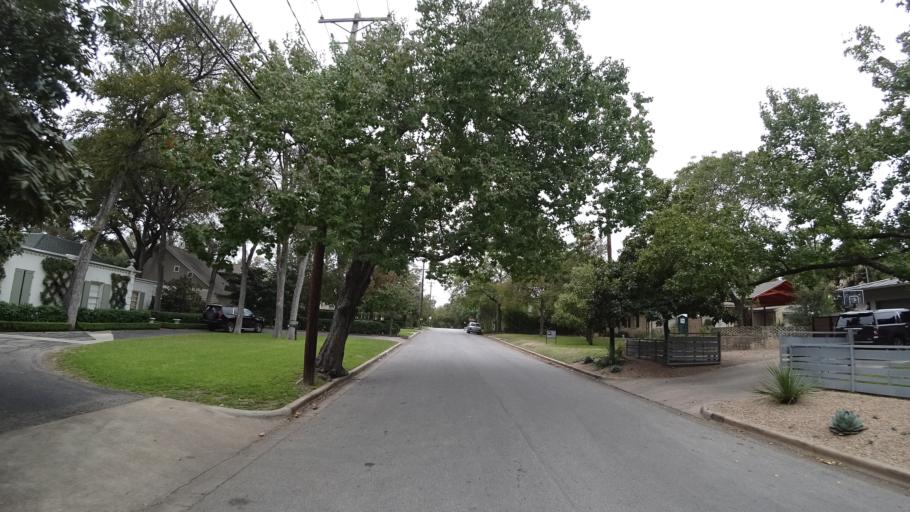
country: US
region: Texas
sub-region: Travis County
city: Rollingwood
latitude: 30.2985
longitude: -97.7688
